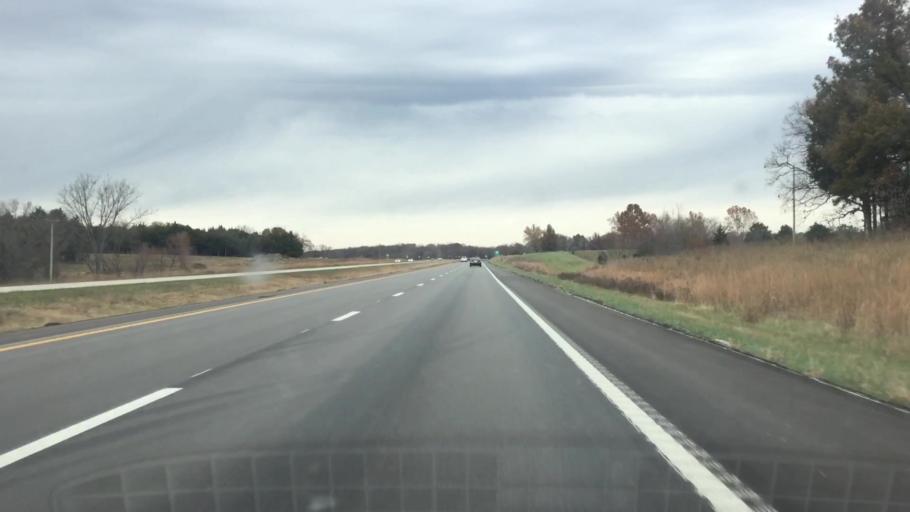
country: US
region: Missouri
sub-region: Saint Clair County
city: Osceola
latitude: 38.0037
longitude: -93.6558
